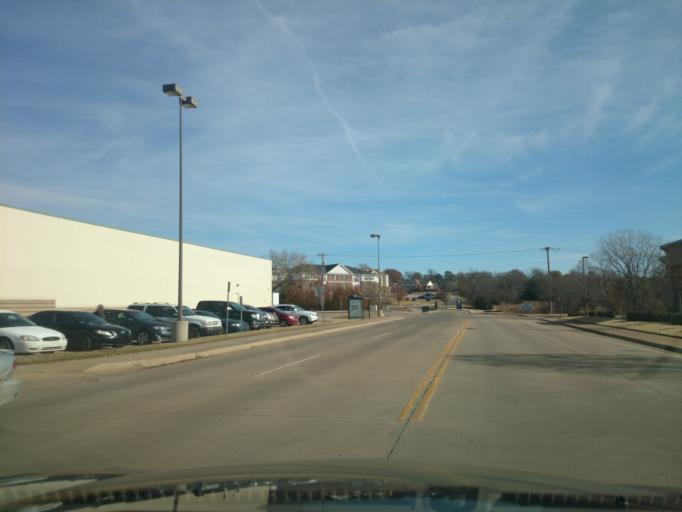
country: US
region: Oklahoma
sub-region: Payne County
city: Stillwater
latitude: 36.1269
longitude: -97.0501
